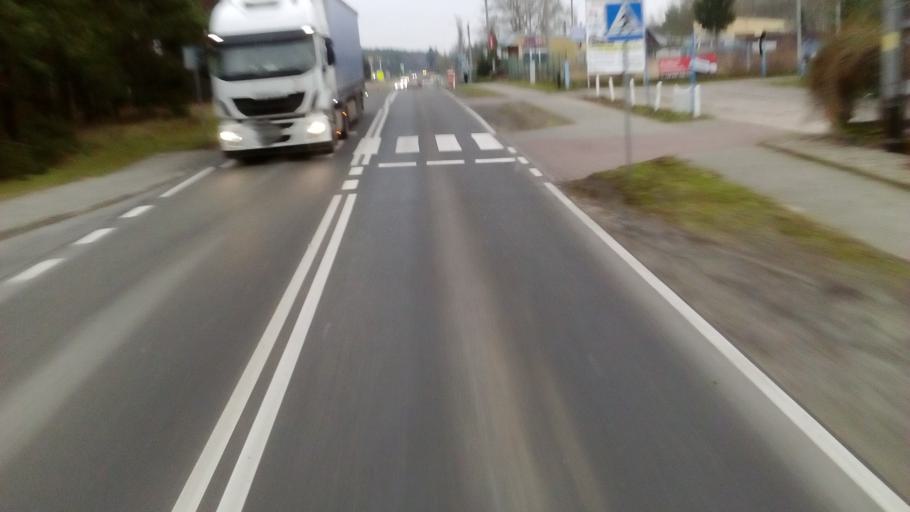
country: PL
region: West Pomeranian Voivodeship
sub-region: Powiat policki
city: Dobra
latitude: 53.4504
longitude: 14.3855
